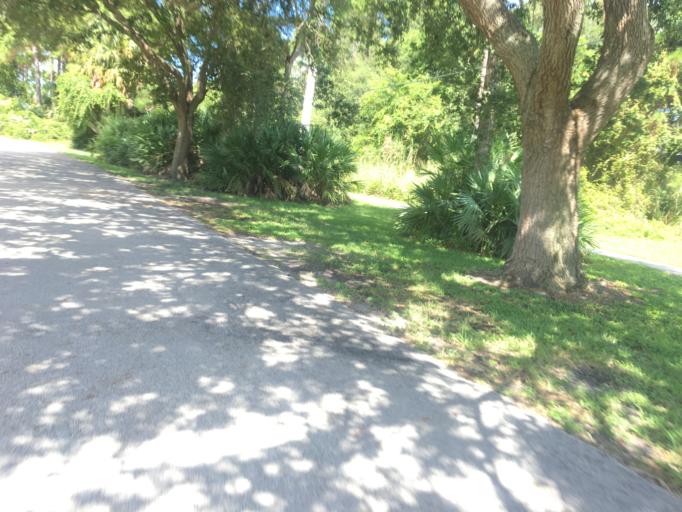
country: US
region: Florida
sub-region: Martin County
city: Palm City
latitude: 27.1791
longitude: -80.2726
